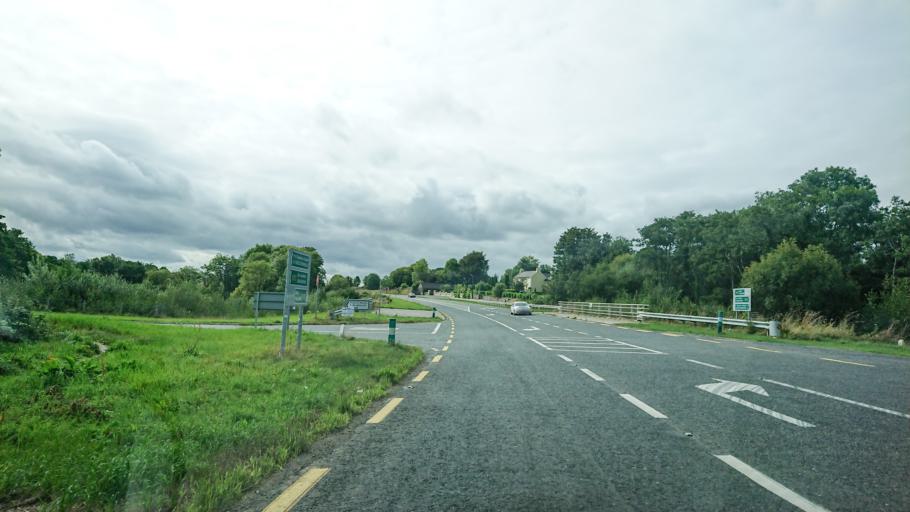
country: IE
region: Munster
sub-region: County Cork
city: Mallow
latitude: 52.1556
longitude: -8.5094
